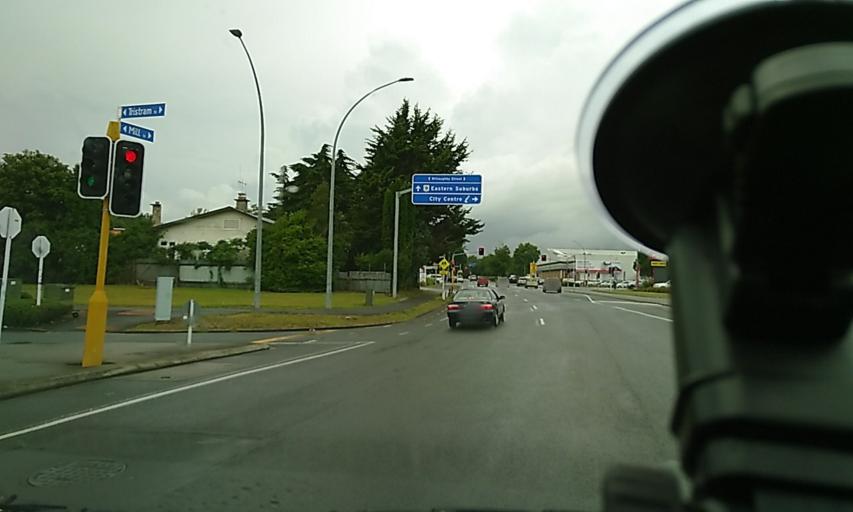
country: NZ
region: Waikato
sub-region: Hamilton City
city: Hamilton
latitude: -37.7814
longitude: 175.2711
